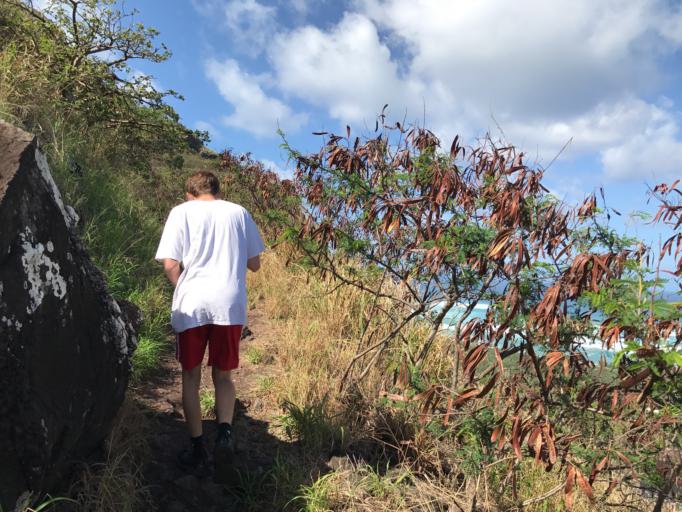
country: US
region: Hawaii
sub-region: Honolulu County
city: Mokuleia
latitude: 21.5739
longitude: -158.2102
